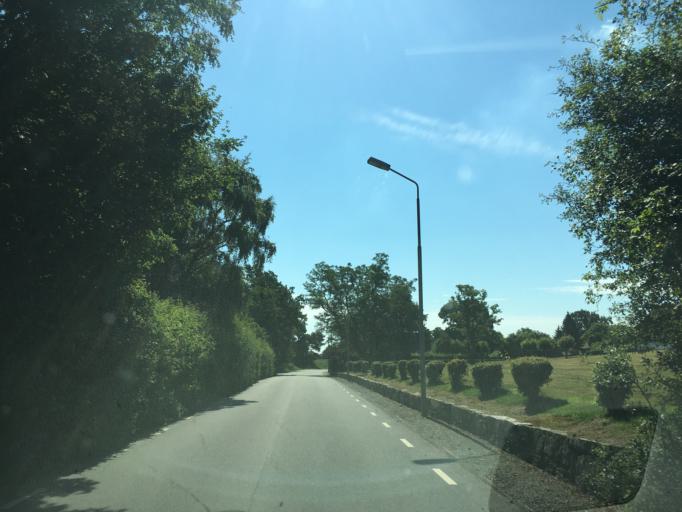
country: SE
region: Skane
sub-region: Simrishamns Kommun
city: Simrishamn
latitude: 55.5952
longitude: 14.3085
